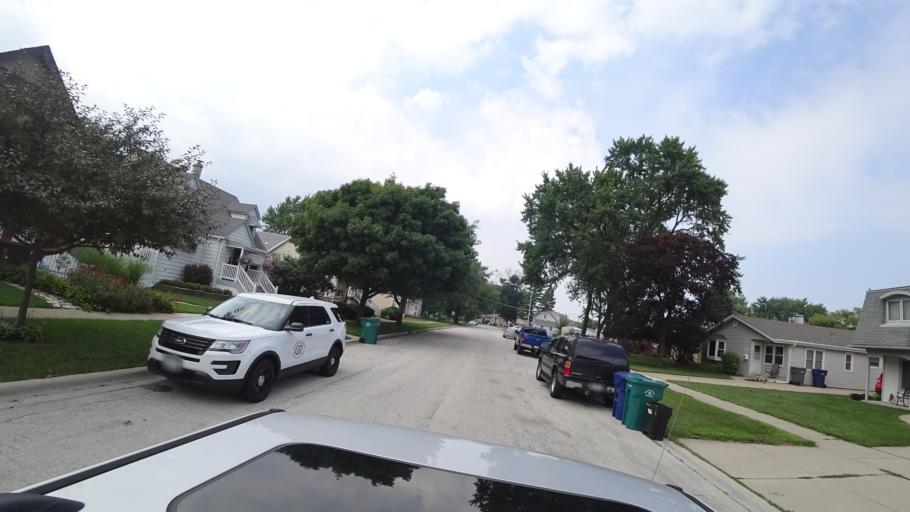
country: US
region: Illinois
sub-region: Cook County
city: Chicago Ridge
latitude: 41.7005
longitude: -87.7768
